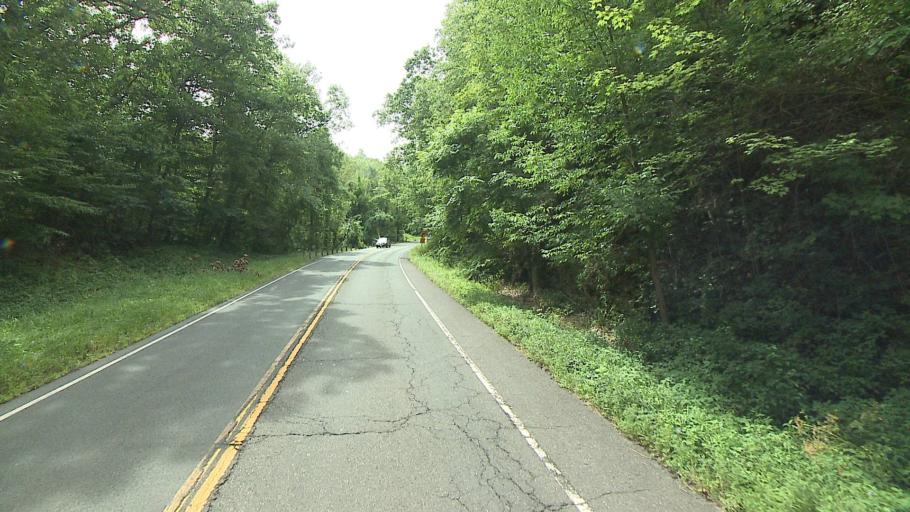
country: US
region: Connecticut
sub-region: Fairfield County
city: Newtown
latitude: 41.4764
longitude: -73.3510
